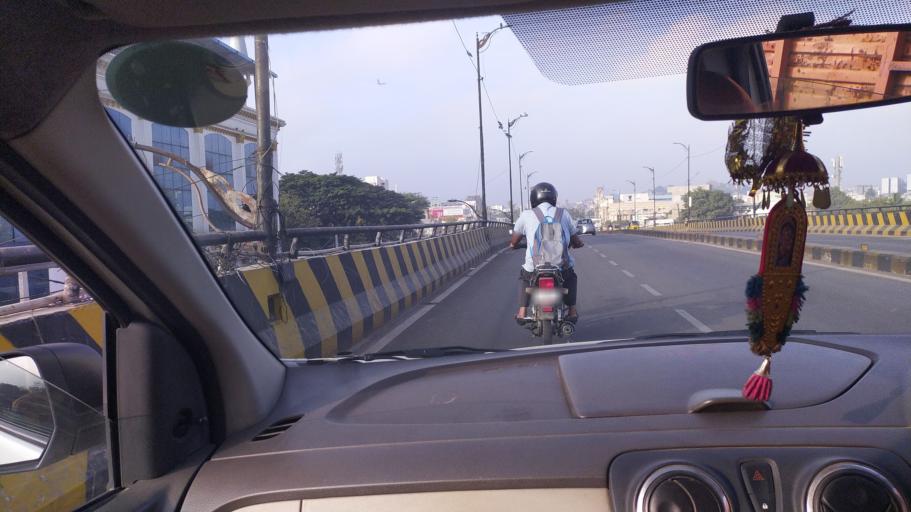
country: IN
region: Telangana
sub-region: Rangareddi
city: Balapur
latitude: 17.3266
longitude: 78.4765
